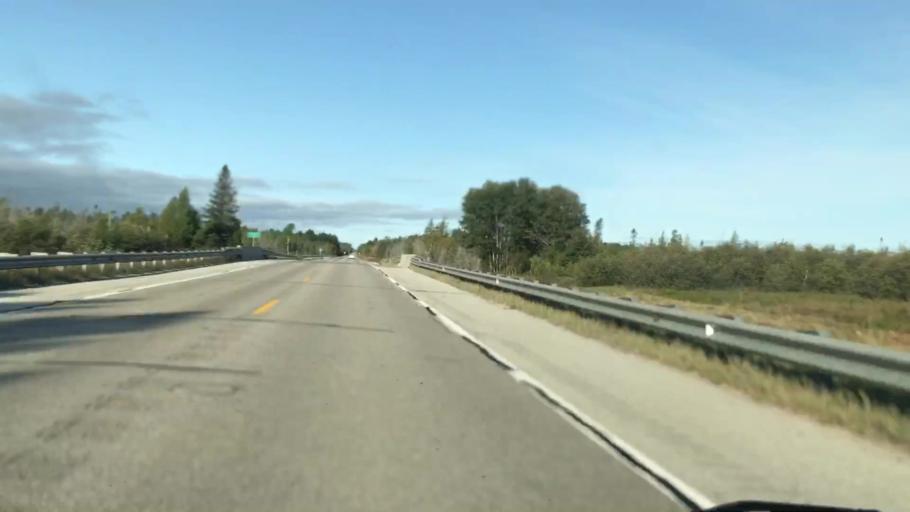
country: US
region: Michigan
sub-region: Luce County
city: Newberry
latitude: 46.3036
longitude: -85.3215
